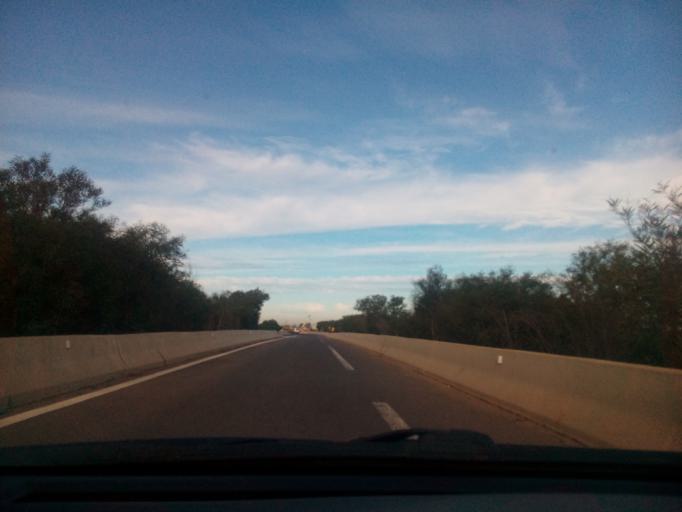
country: DZ
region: Mascara
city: Mascara
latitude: 35.6253
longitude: 0.0746
